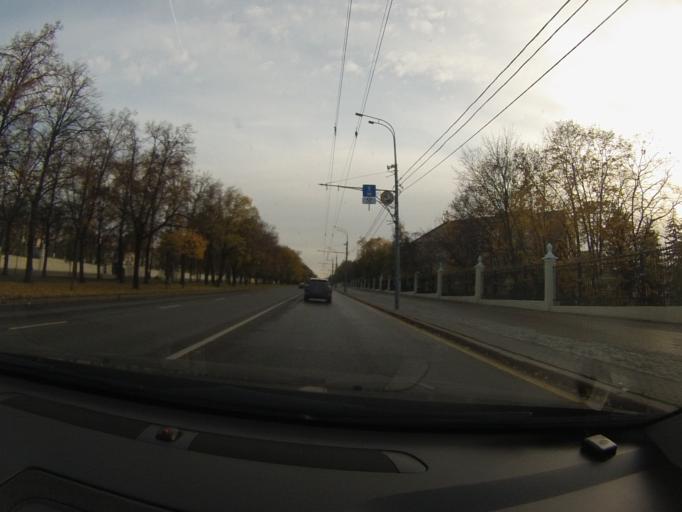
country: RU
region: Moscow
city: Vorob'yovo
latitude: 55.7228
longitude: 37.5346
